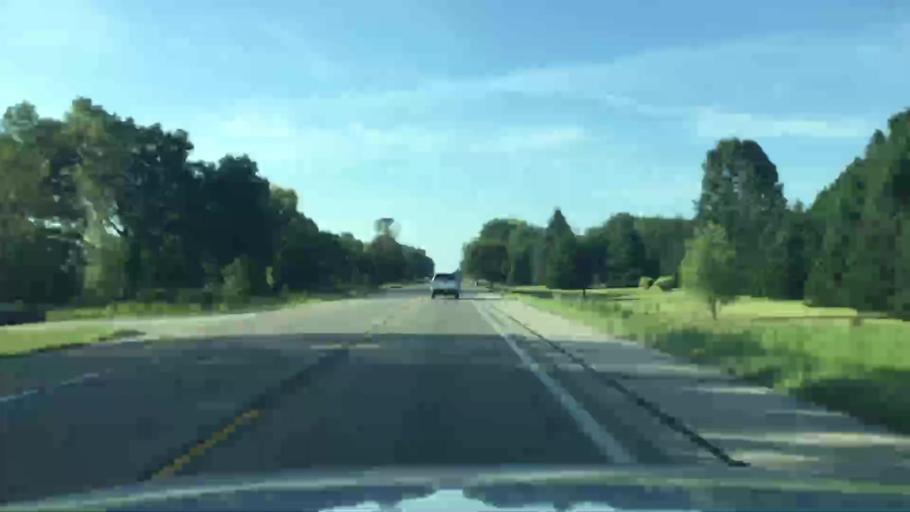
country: US
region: Michigan
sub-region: Jackson County
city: Vandercook Lake
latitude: 42.1092
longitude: -84.3640
